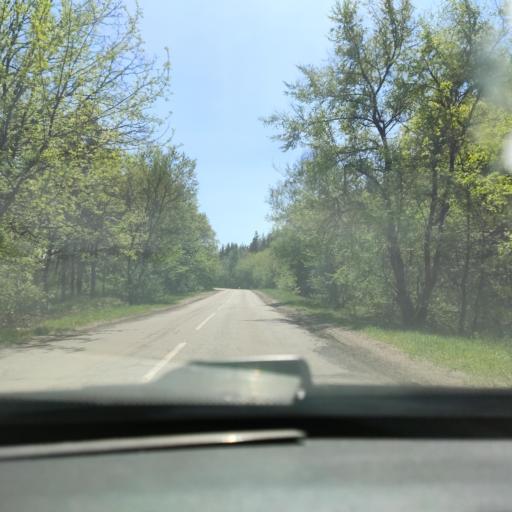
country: RU
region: Voronezj
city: Somovo
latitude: 51.7158
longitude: 39.3668
